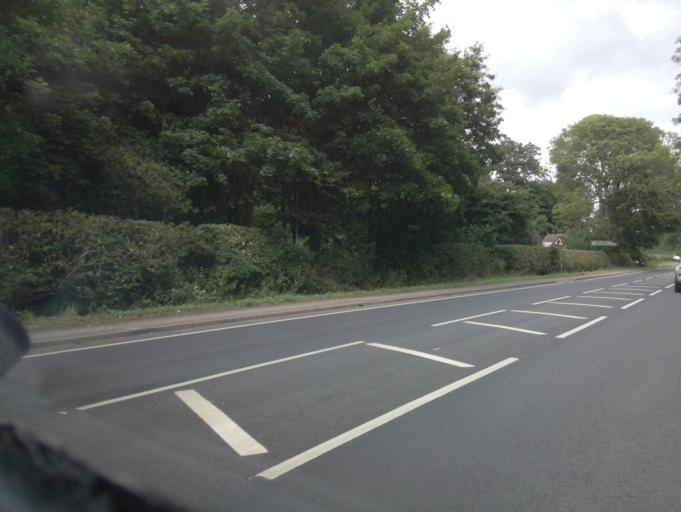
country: GB
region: England
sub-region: Nottinghamshire
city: Burton Joyce
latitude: 52.9949
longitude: -1.0243
